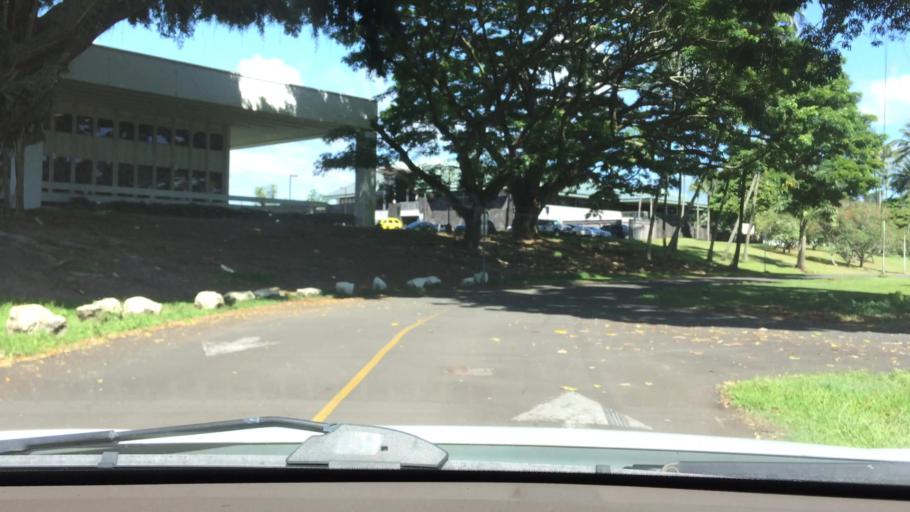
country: US
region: Hawaii
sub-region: Hawaii County
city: Hilo
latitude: 19.7193
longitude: -155.0766
